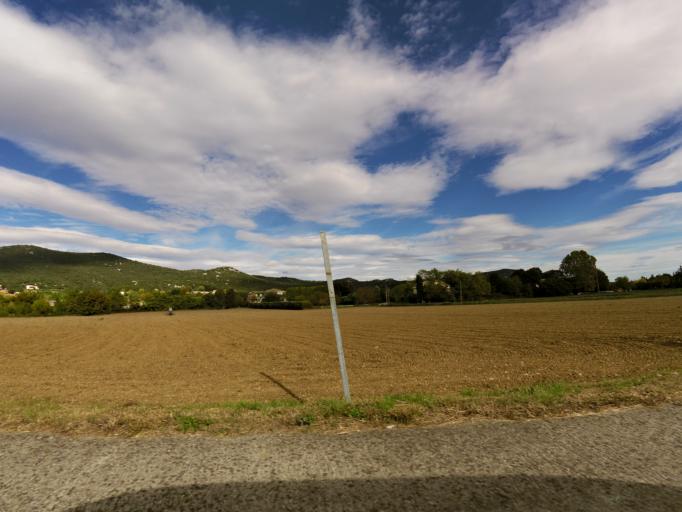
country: FR
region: Languedoc-Roussillon
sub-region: Departement du Gard
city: Saint-Hippolyte-du-Fort
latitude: 43.9593
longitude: 3.8600
